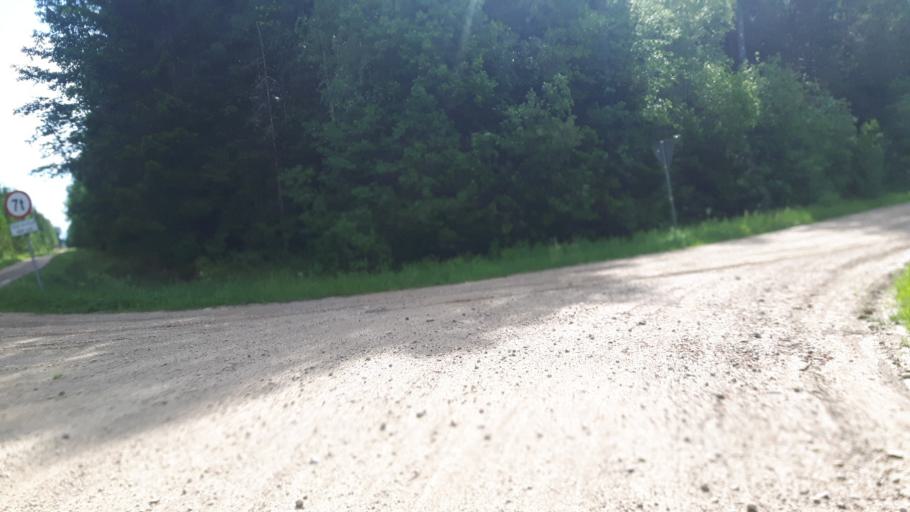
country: EE
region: Paernumaa
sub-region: Vaendra vald (alev)
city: Vandra
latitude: 58.7305
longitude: 25.0284
